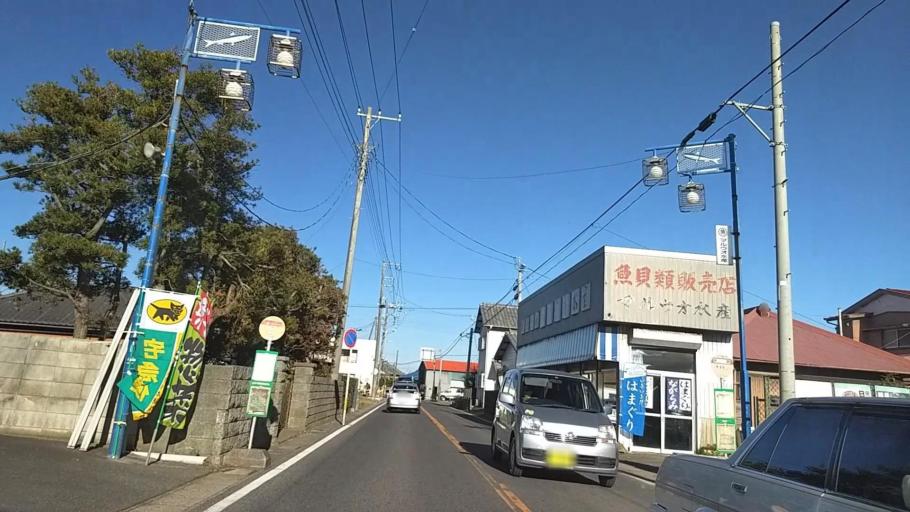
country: JP
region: Chiba
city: Naruto
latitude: 35.5400
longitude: 140.4533
